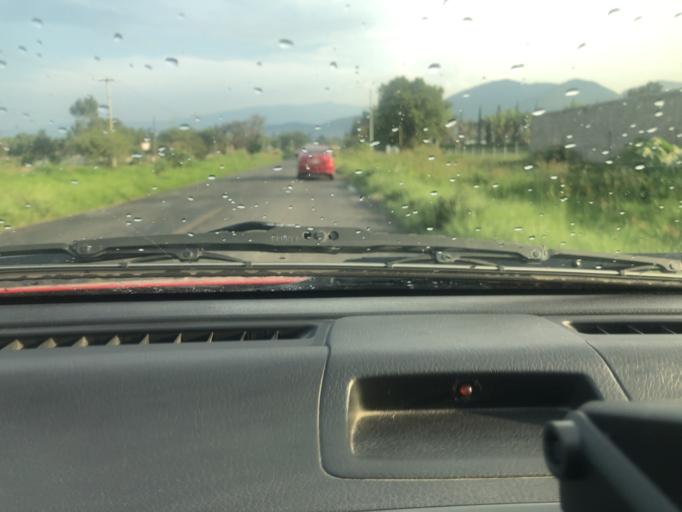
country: MX
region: Jalisco
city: Santa Cruz del Valle
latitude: 20.5474
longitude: -103.4206
